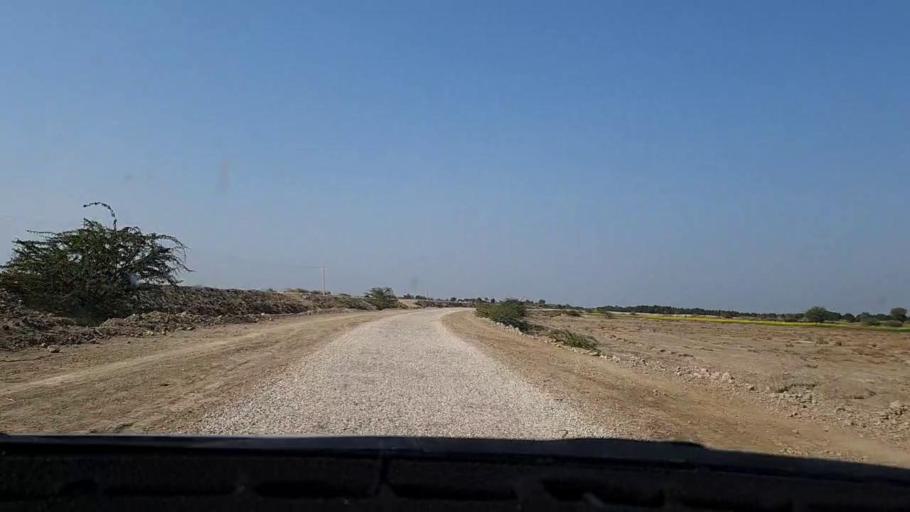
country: PK
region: Sindh
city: Tando Mittha Khan
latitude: 25.8208
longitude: 69.2940
